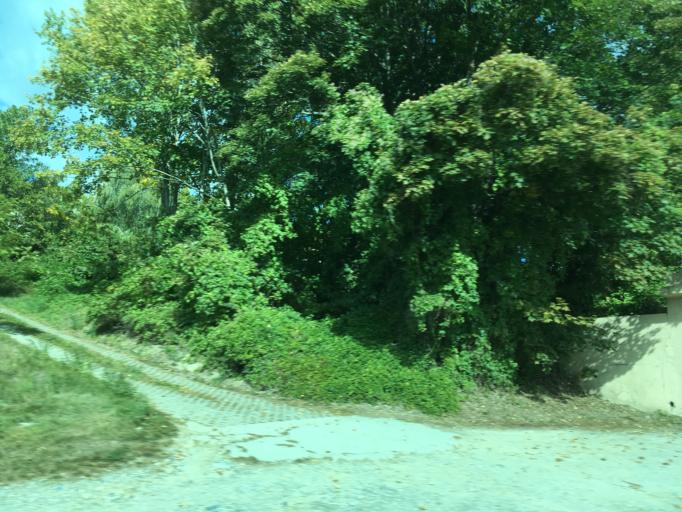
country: CH
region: Valais
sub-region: Sierre District
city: Chermignon-d'en Haut
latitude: 46.2945
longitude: 7.4861
